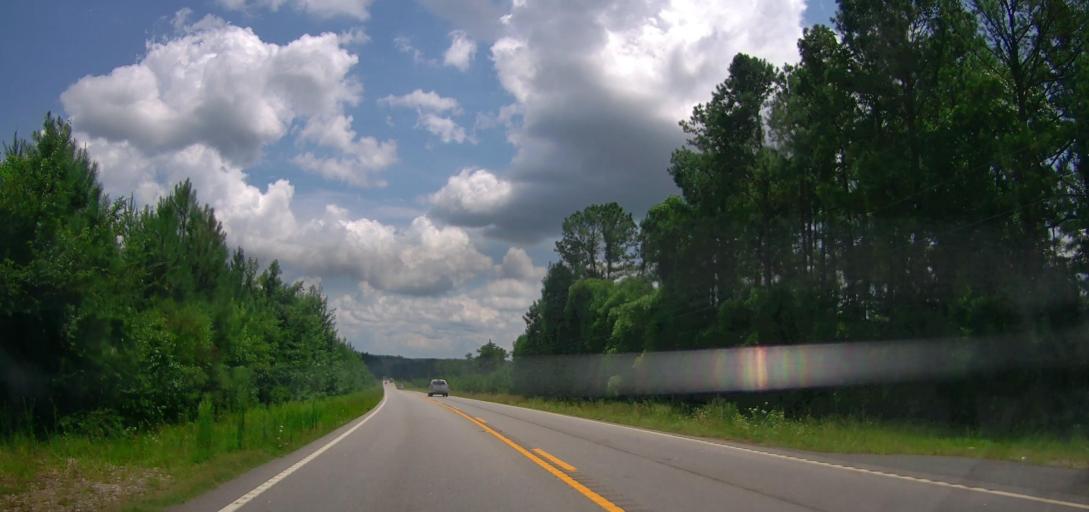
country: US
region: Georgia
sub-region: Meriwether County
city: Greenville
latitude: 33.0236
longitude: -84.6852
